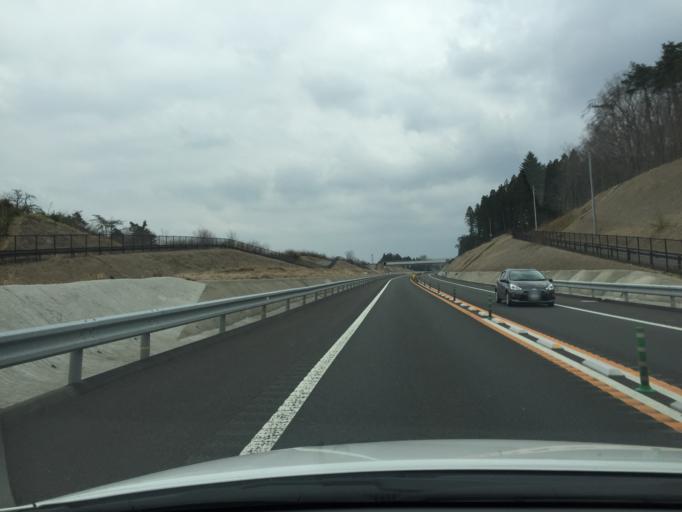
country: JP
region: Miyagi
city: Marumori
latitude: 37.8713
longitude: 140.8825
